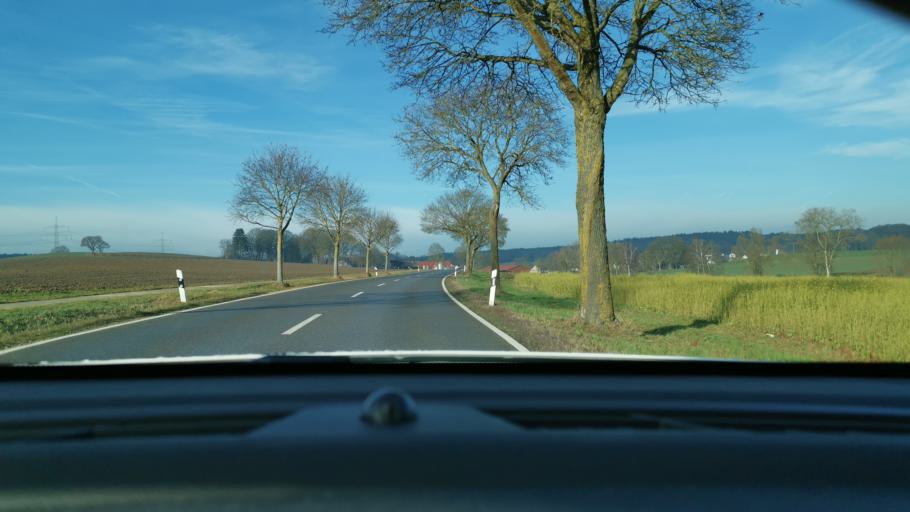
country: DE
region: Bavaria
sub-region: Swabia
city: Hollenbach
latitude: 48.5002
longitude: 11.0709
